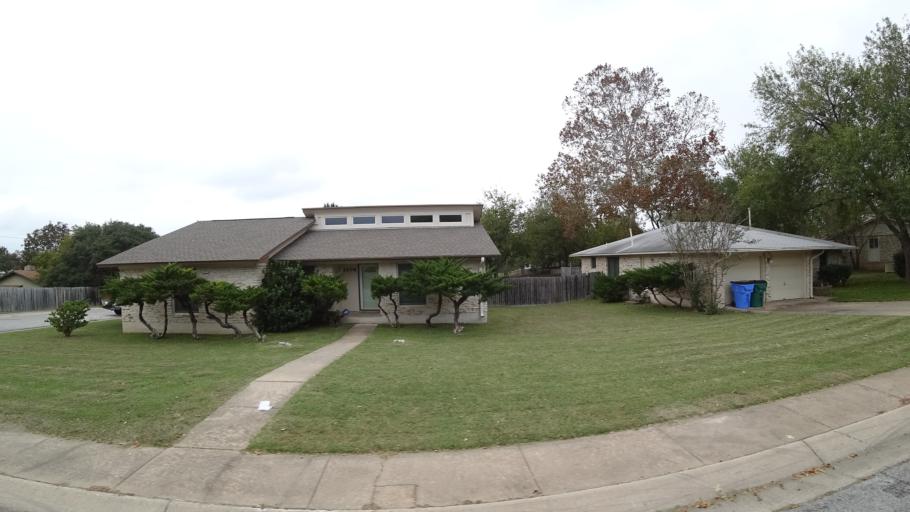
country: US
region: Texas
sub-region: Travis County
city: Pflugerville
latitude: 30.4299
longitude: -97.6126
